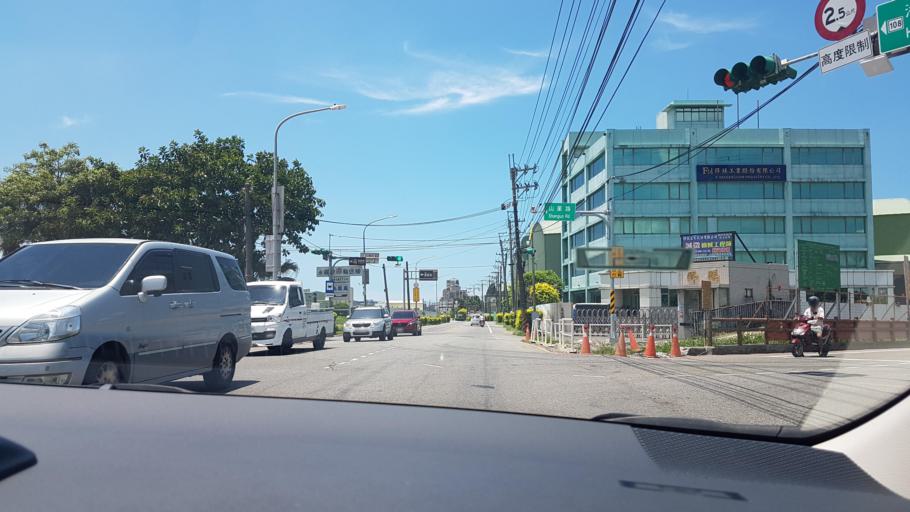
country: TW
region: Taiwan
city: Taoyuan City
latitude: 25.0907
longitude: 121.2746
